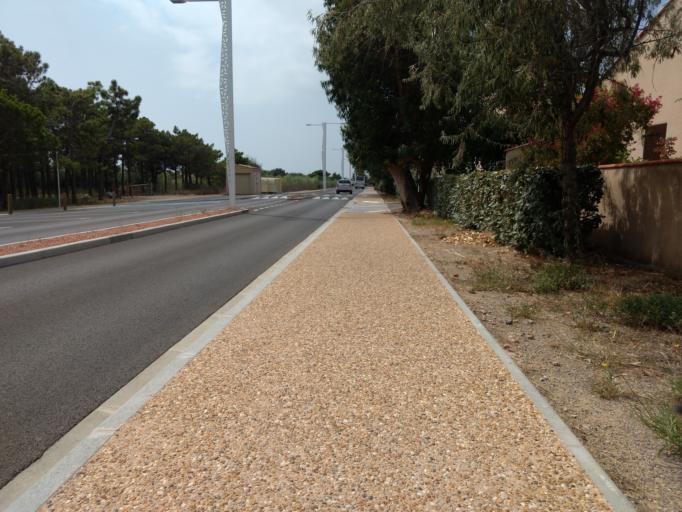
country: FR
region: Languedoc-Roussillon
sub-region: Departement des Pyrenees-Orientales
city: Le Barcares
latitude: 42.8435
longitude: 3.0368
